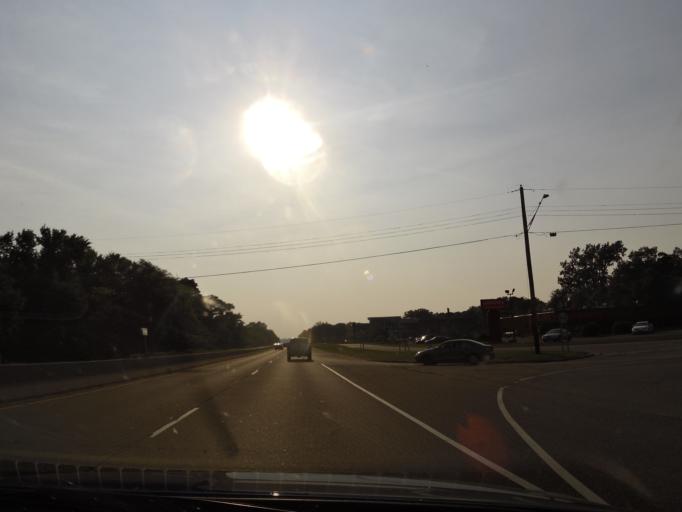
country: US
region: Minnesota
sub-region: Hennepin County
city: Hopkins
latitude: 44.9214
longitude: -93.4726
